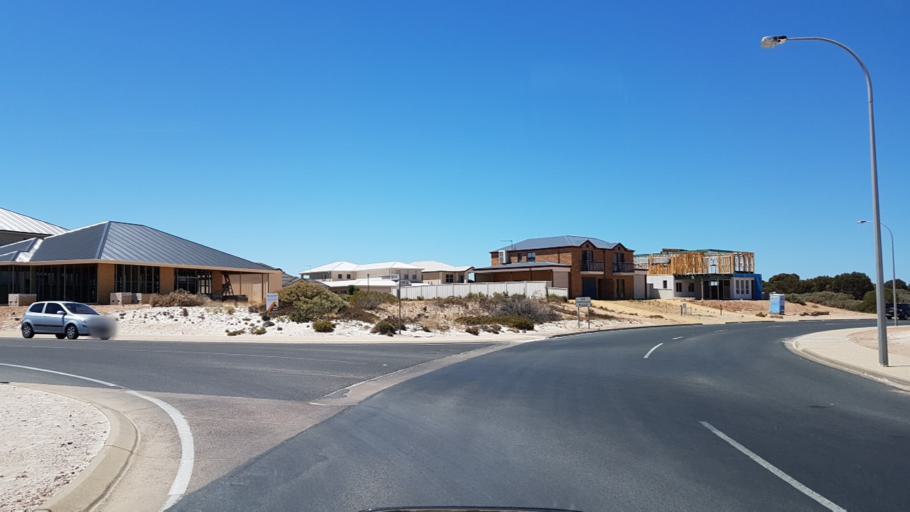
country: AU
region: South Australia
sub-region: Copper Coast
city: Wallaroo
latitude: -33.9184
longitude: 137.6329
